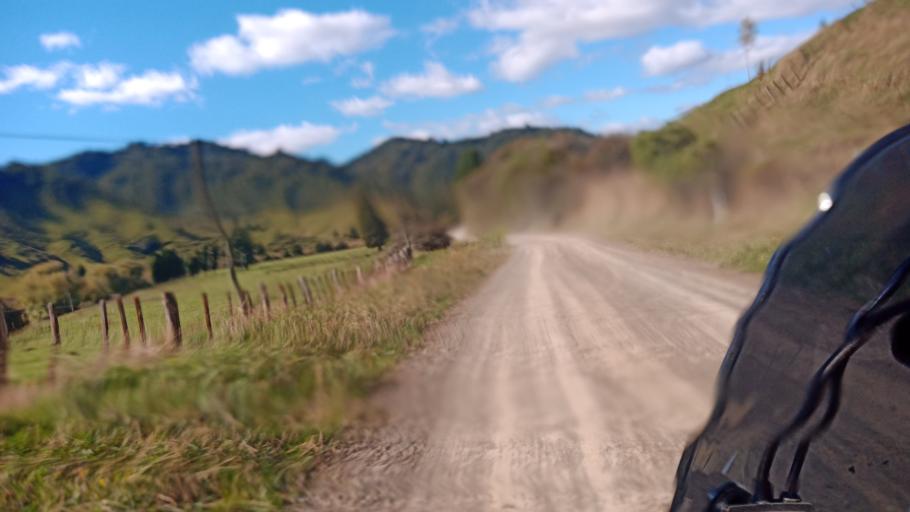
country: NZ
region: Bay of Plenty
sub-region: Opotiki District
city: Opotiki
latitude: -38.2533
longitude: 177.5806
